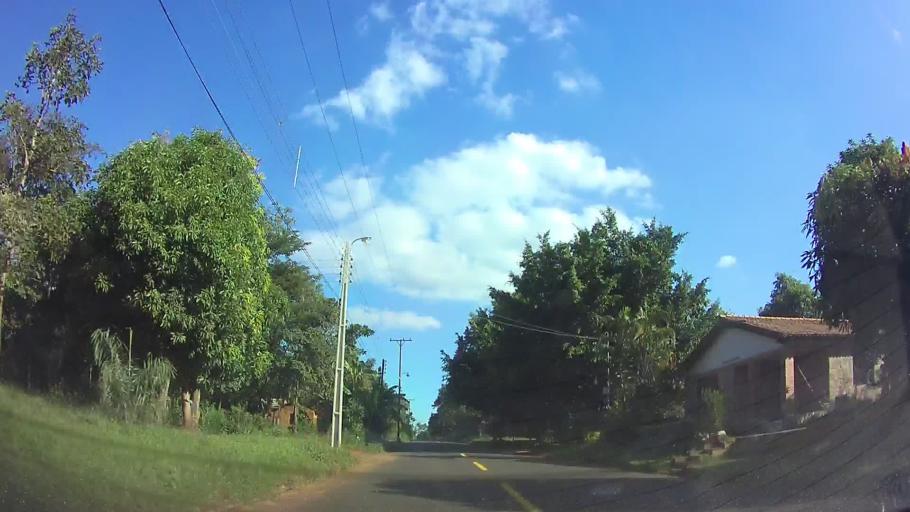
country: PY
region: Central
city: Aregua
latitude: -25.2673
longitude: -57.4363
